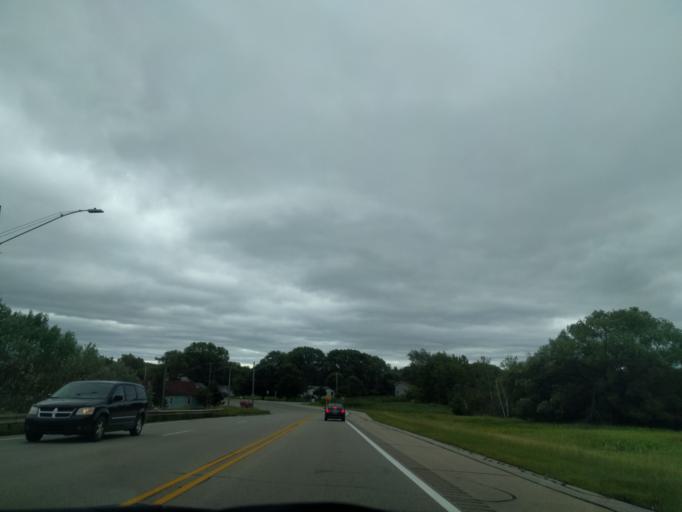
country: US
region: Michigan
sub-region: Delta County
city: Gladstone
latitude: 45.8537
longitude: -87.0339
